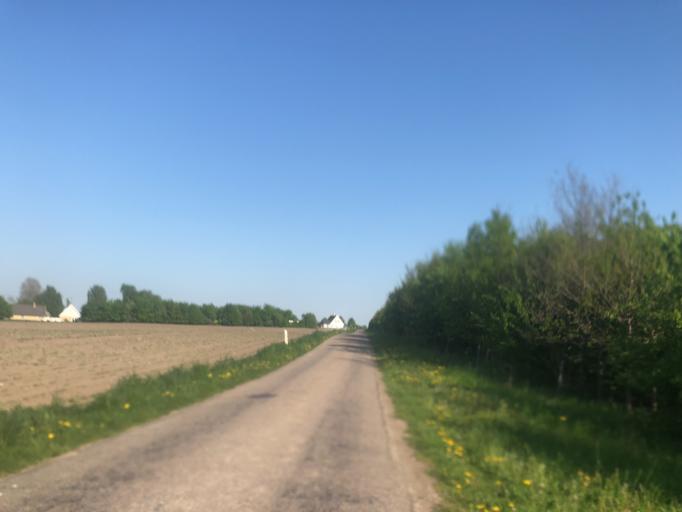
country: DK
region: Zealand
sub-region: Ringsted Kommune
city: Ringsted
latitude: 55.4742
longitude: 11.8183
